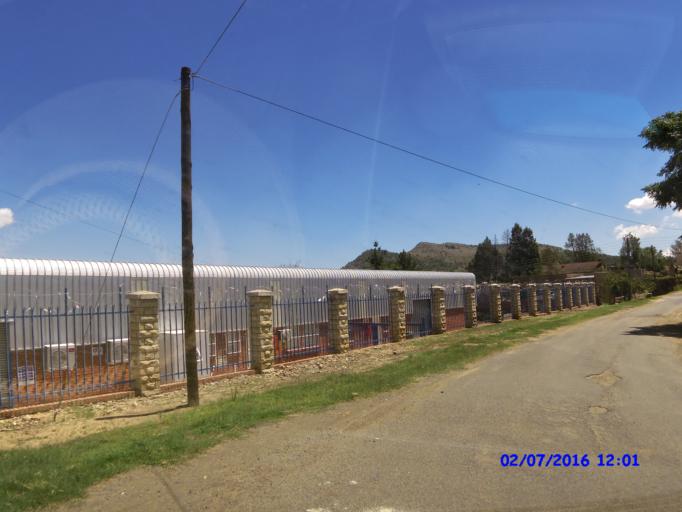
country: LS
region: Maseru
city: Maseru
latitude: -29.3032
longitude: 27.4597
